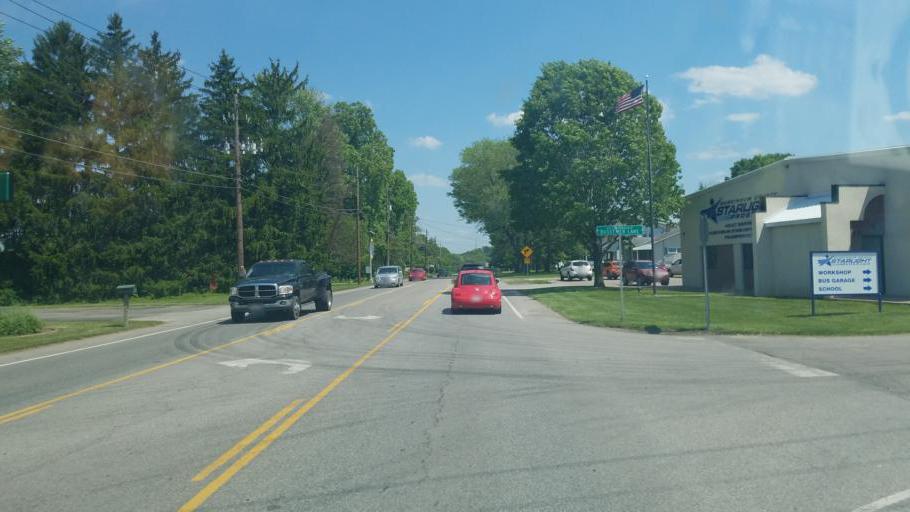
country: US
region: Ohio
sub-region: Muskingum County
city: Zanesville
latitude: 39.9586
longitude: -82.0286
